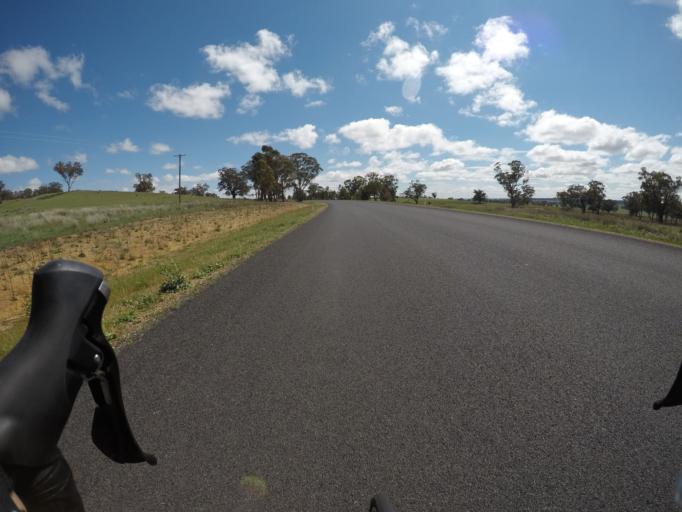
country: AU
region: New South Wales
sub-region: Dubbo Municipality
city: Dubbo
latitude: -32.5145
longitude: 148.5553
